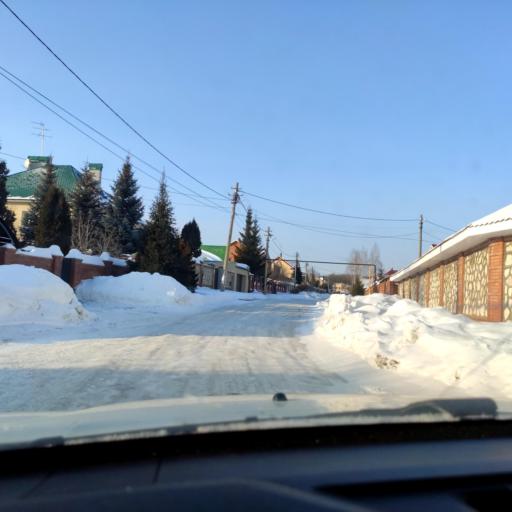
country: RU
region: Samara
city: Petra-Dubrava
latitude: 53.3202
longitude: 50.2870
